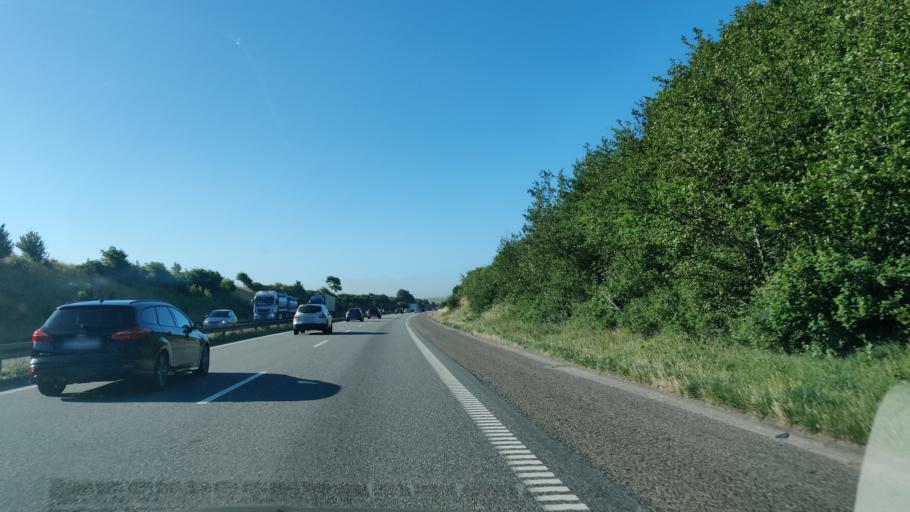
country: DK
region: Central Jutland
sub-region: Randers Kommune
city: Assentoft
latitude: 56.4001
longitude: 10.0949
